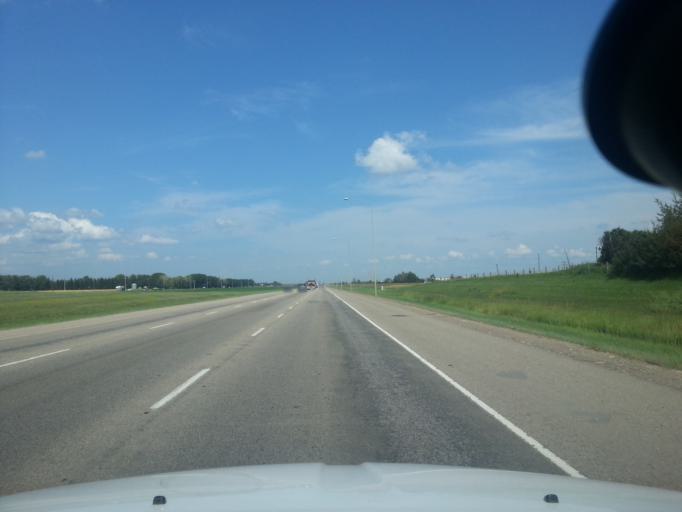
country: CA
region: Alberta
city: Leduc
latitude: 53.3531
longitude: -113.5389
